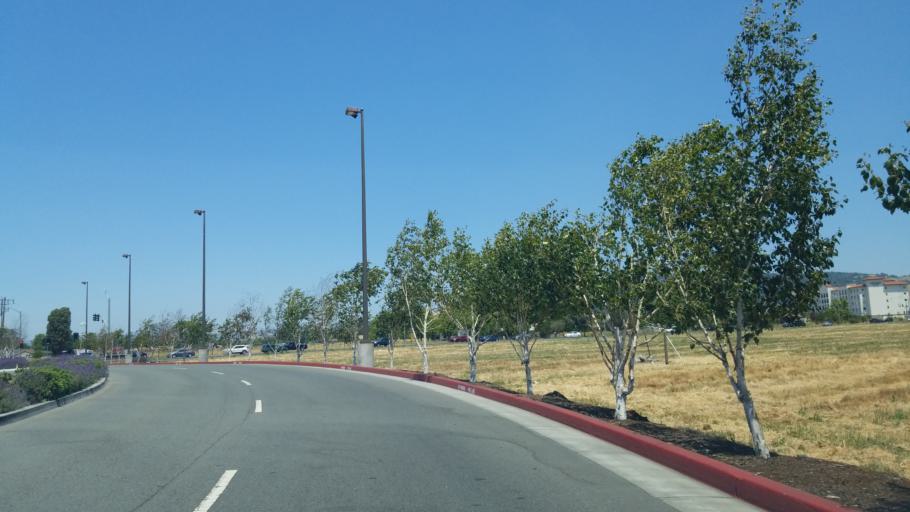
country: US
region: California
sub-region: Sonoma County
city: Rohnert Park
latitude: 38.3620
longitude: -122.7213
